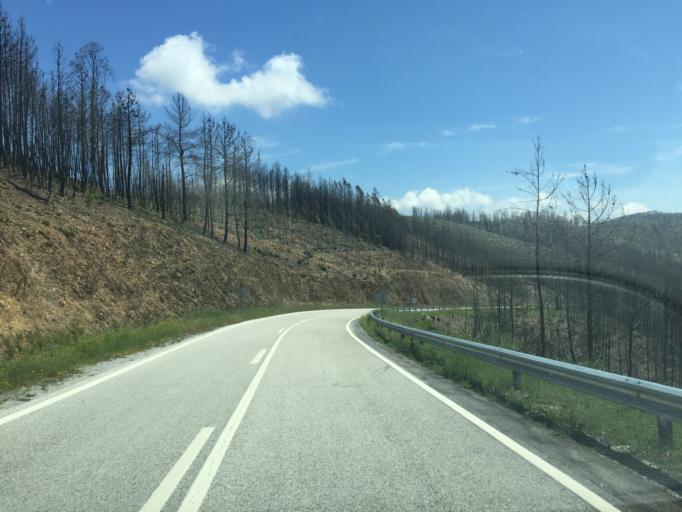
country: PT
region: Coimbra
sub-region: Pampilhosa da Serra
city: Pampilhosa da Serra
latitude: 40.0069
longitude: -7.9893
